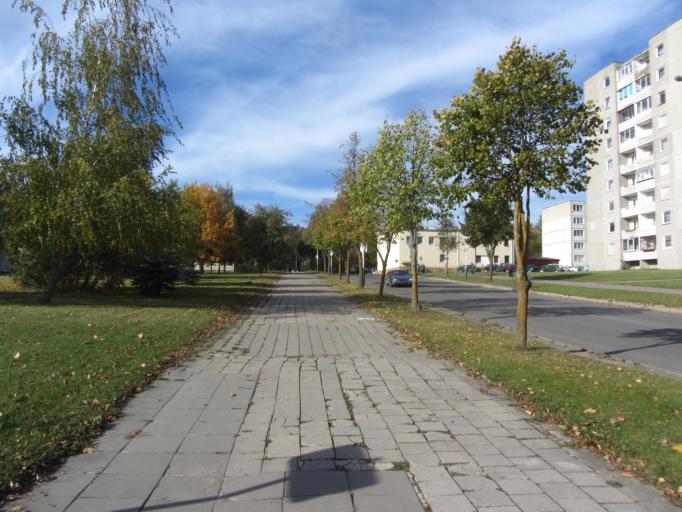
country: LT
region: Vilnius County
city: Elektrenai
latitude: 54.7845
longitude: 24.6672
